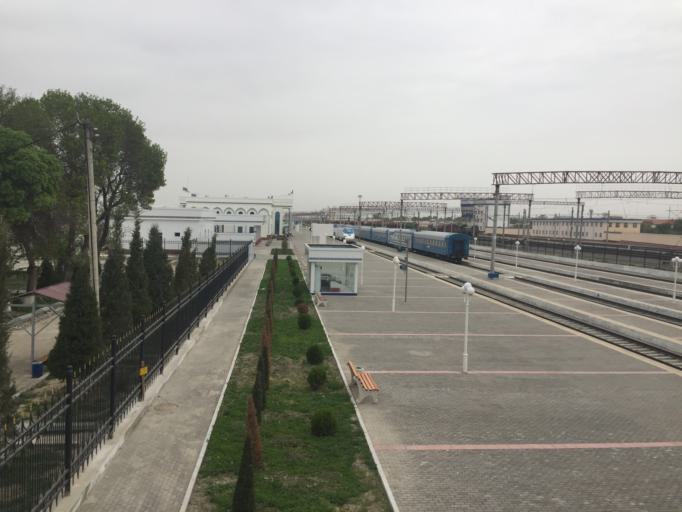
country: UZ
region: Bukhara
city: Kogon
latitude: 39.7213
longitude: 64.5471
